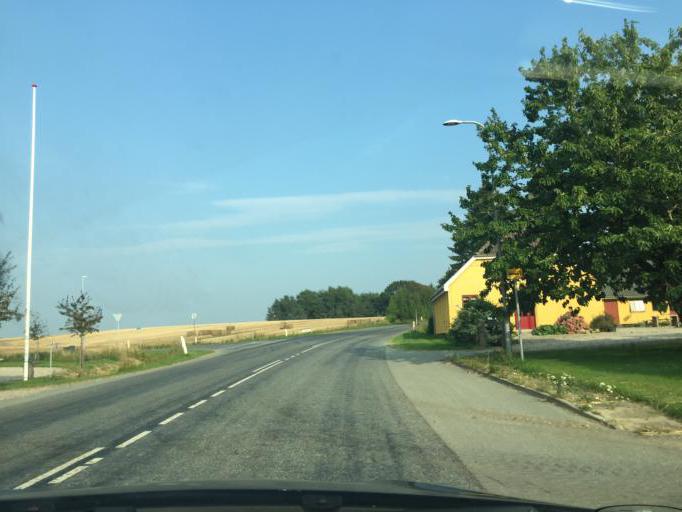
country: DK
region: South Denmark
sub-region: Faaborg-Midtfyn Kommune
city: Arslev
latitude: 55.2850
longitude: 10.4739
